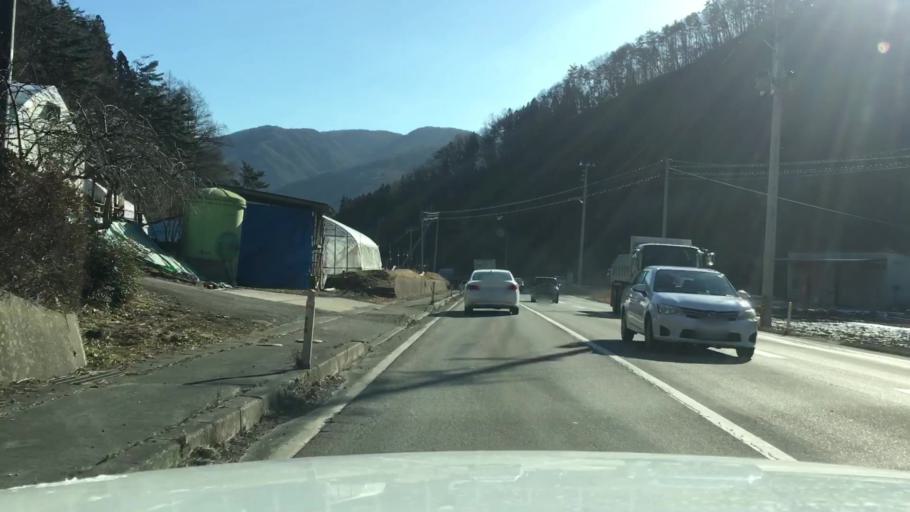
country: JP
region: Iwate
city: Miyako
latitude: 39.5974
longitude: 141.6491
